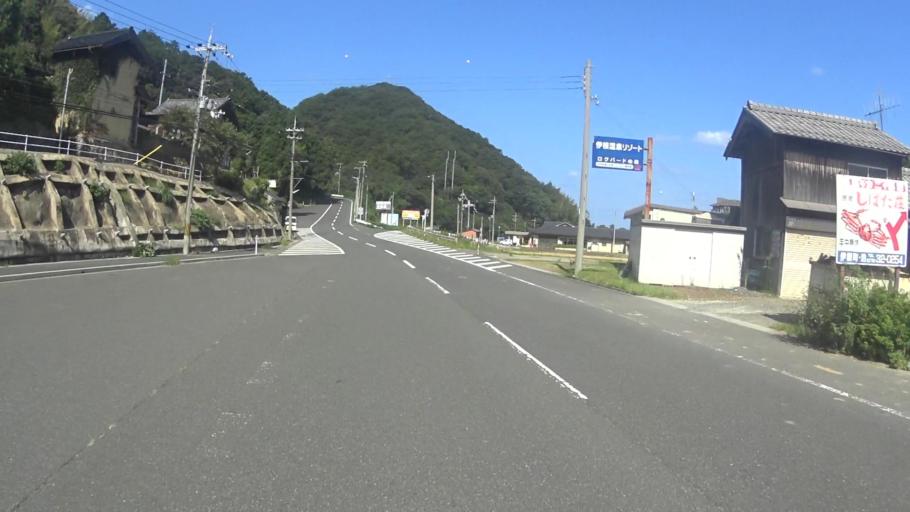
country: JP
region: Kyoto
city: Miyazu
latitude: 35.7030
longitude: 135.2815
